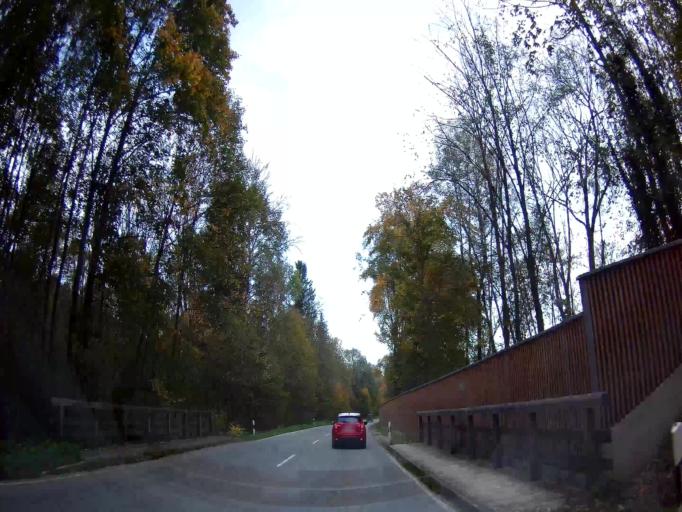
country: DE
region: Bavaria
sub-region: Upper Bavaria
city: Piding
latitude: 47.7559
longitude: 12.9187
